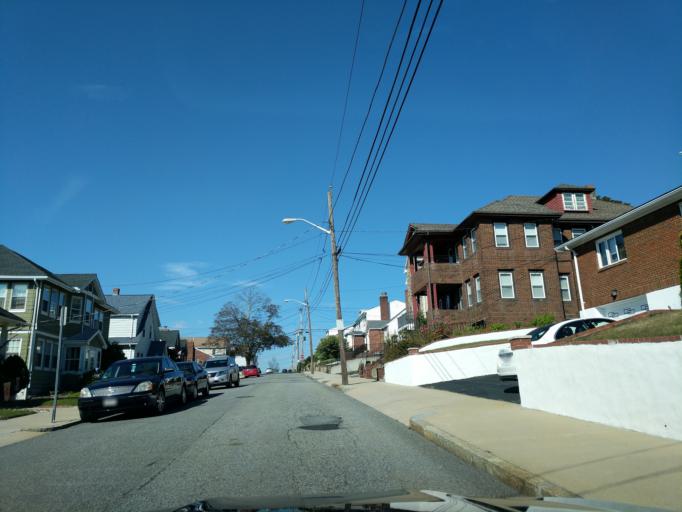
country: US
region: Massachusetts
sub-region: Suffolk County
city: Revere
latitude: 42.4078
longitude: -71.0196
